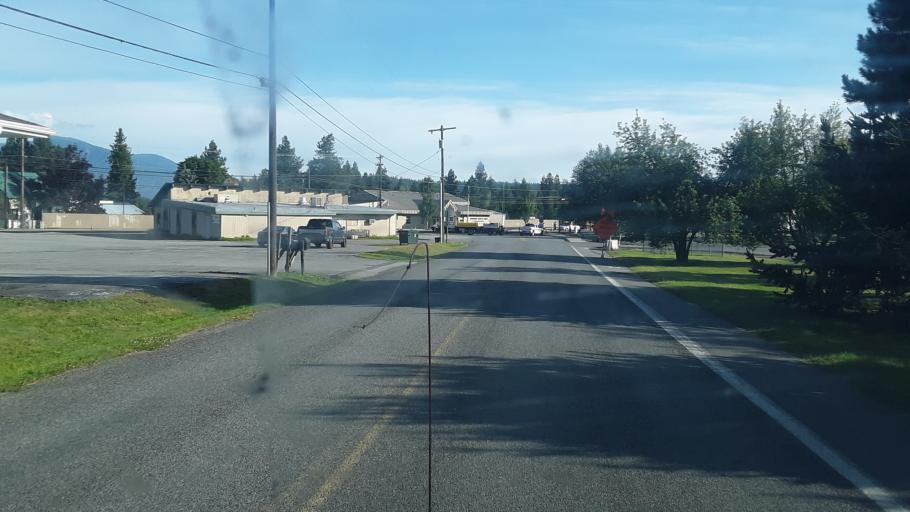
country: US
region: Idaho
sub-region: Boundary County
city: Bonners Ferry
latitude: 48.6786
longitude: -116.3272
